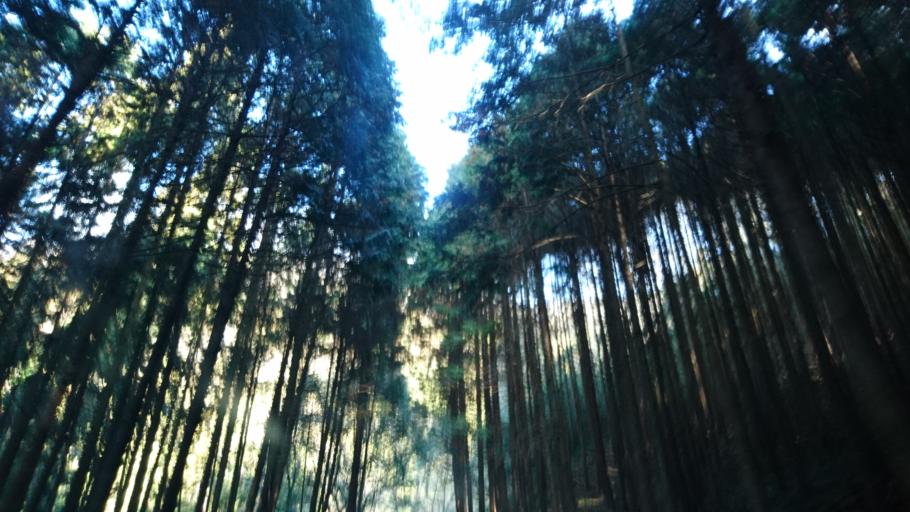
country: JP
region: Okayama
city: Takahashi
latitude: 34.8661
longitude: 133.5710
